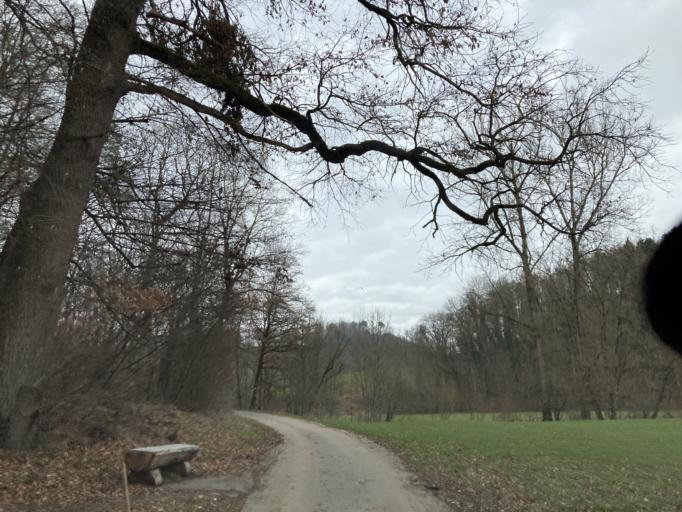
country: DE
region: Baden-Wuerttemberg
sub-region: Tuebingen Region
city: Hirrlingen
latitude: 48.4275
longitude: 8.8622
